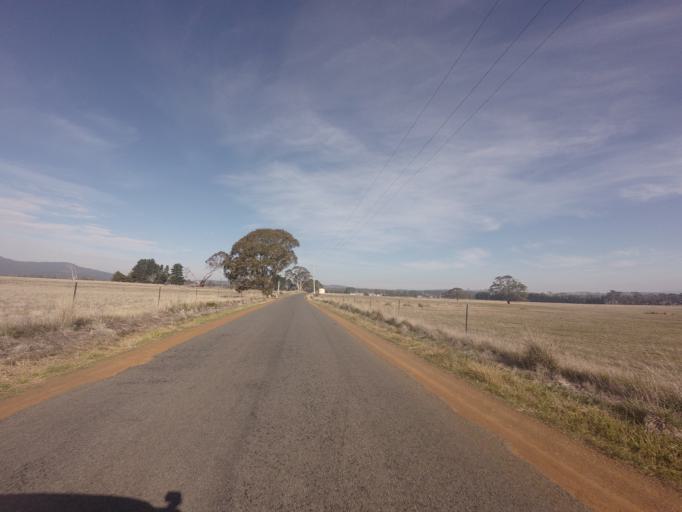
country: AU
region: Tasmania
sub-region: Sorell
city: Sorell
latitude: -42.4345
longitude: 147.4720
